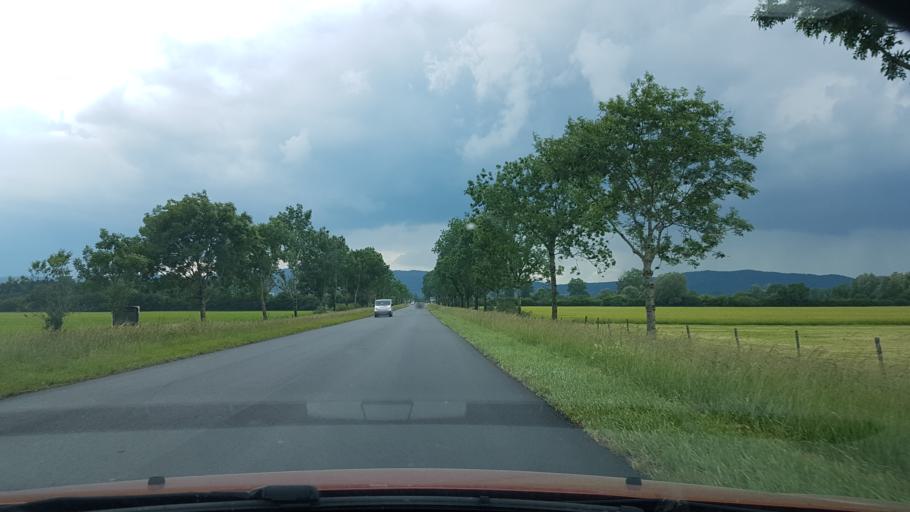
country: FR
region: Franche-Comte
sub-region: Departement du Jura
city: Clairvaux-les-Lacs
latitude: 46.5894
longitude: 5.7269
